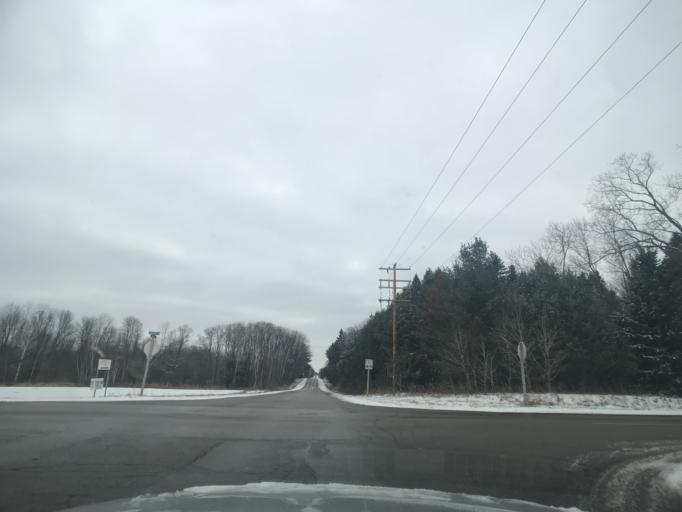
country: US
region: Wisconsin
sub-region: Brown County
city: Suamico
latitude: 44.7064
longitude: -88.0710
